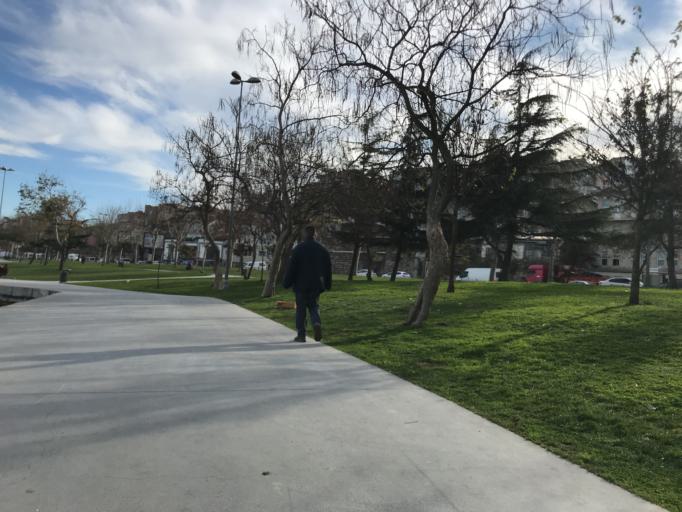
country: TR
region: Istanbul
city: Istanbul
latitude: 41.0294
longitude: 28.9530
